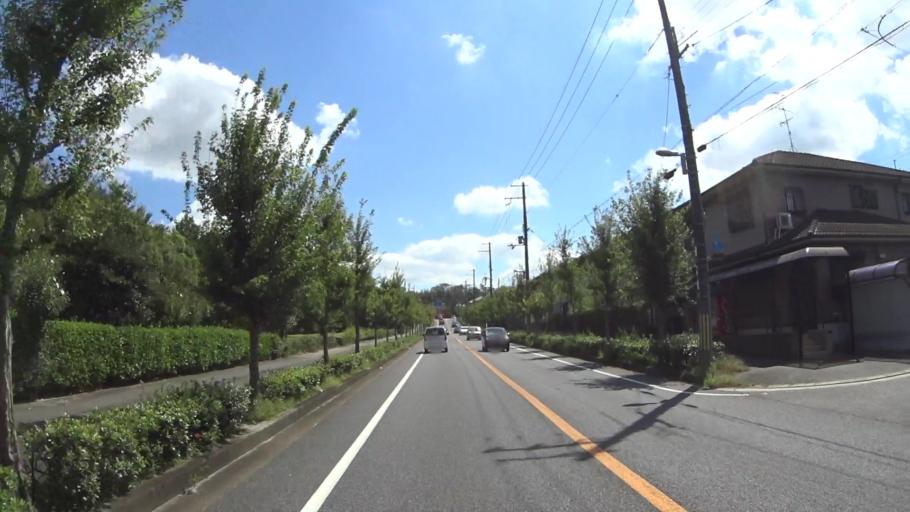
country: JP
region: Kyoto
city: Uji
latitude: 34.8673
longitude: 135.7958
